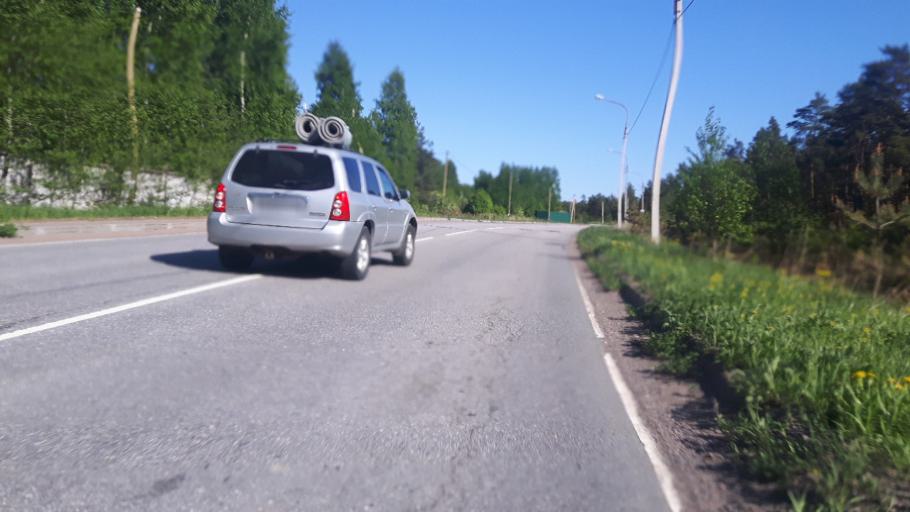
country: RU
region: Leningrad
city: Sosnovyy Bor
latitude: 60.1912
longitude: 29.0132
